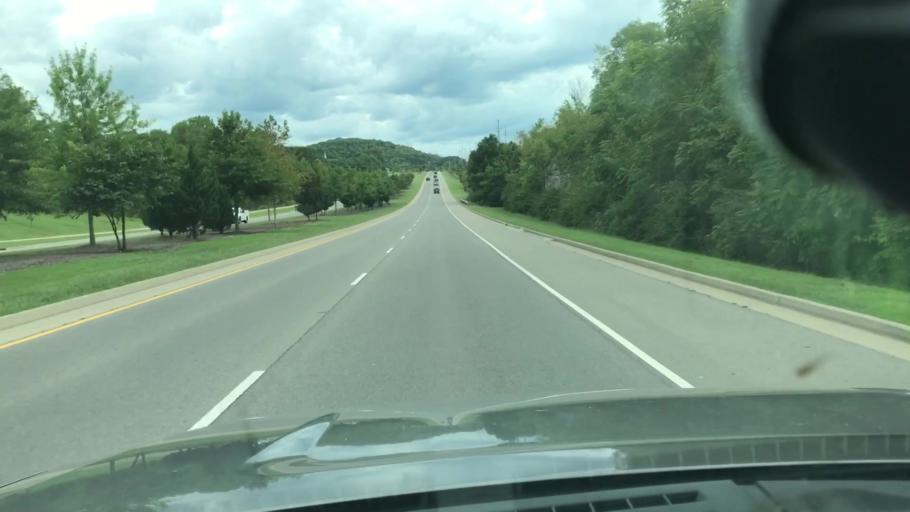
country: US
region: Tennessee
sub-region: Williamson County
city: Franklin
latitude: 35.9206
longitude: -86.8437
